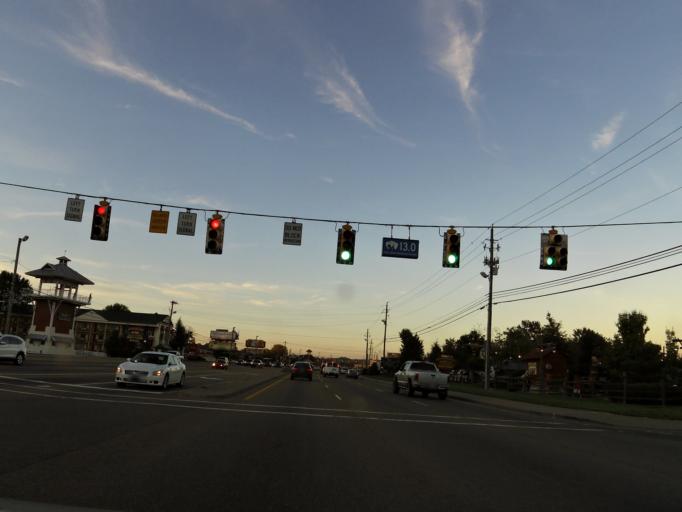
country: US
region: Tennessee
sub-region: Sevier County
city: Sevierville
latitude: 35.8321
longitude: -83.5731
